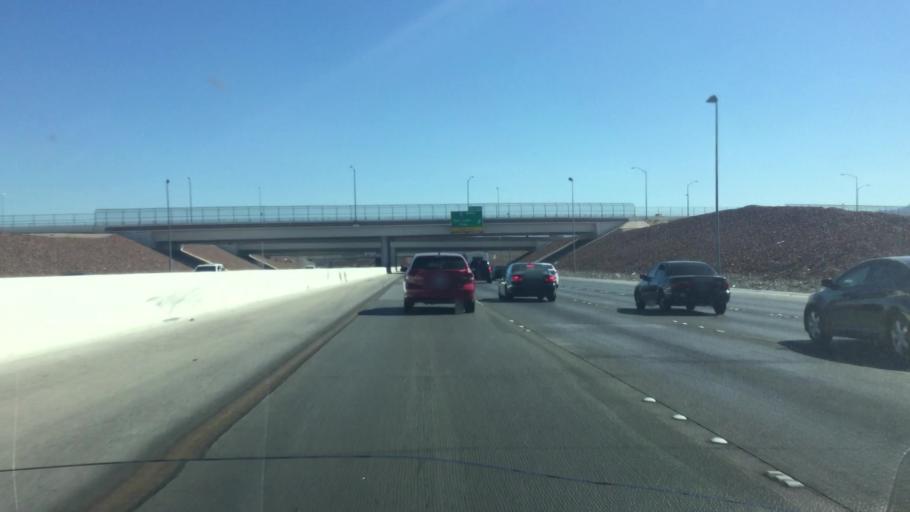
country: US
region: Nevada
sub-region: Clark County
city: Paradise
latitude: 36.0651
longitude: -115.1859
